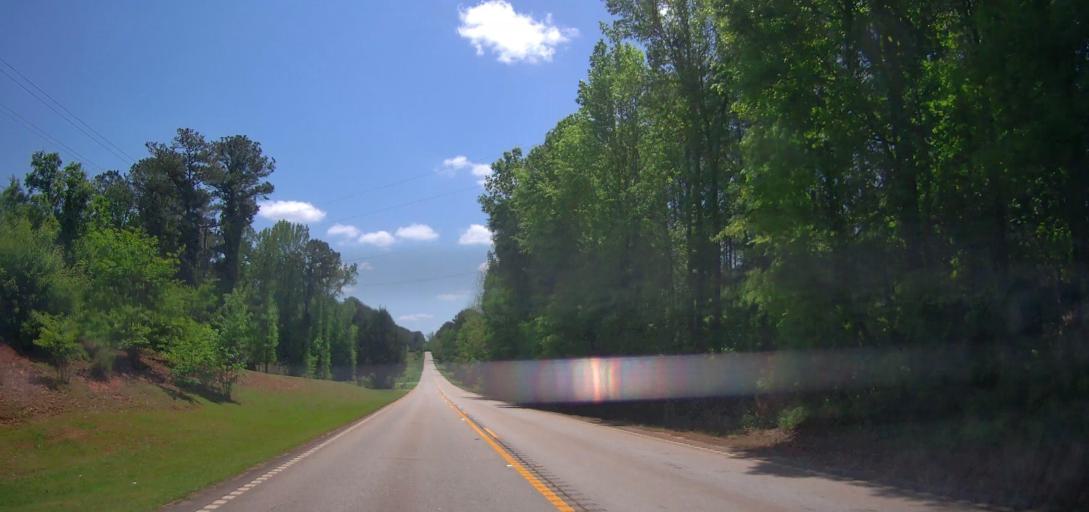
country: US
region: Georgia
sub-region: Jasper County
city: Monticello
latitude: 33.2094
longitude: -83.6628
